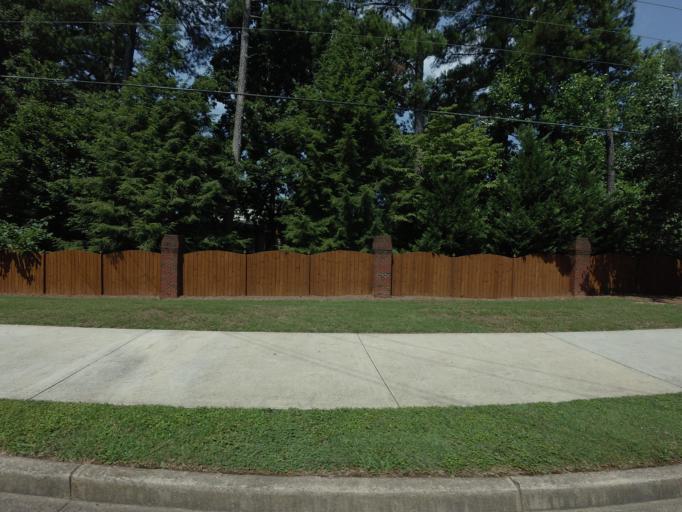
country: US
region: Georgia
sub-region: Fulton County
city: Johns Creek
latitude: 34.0108
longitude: -84.2634
